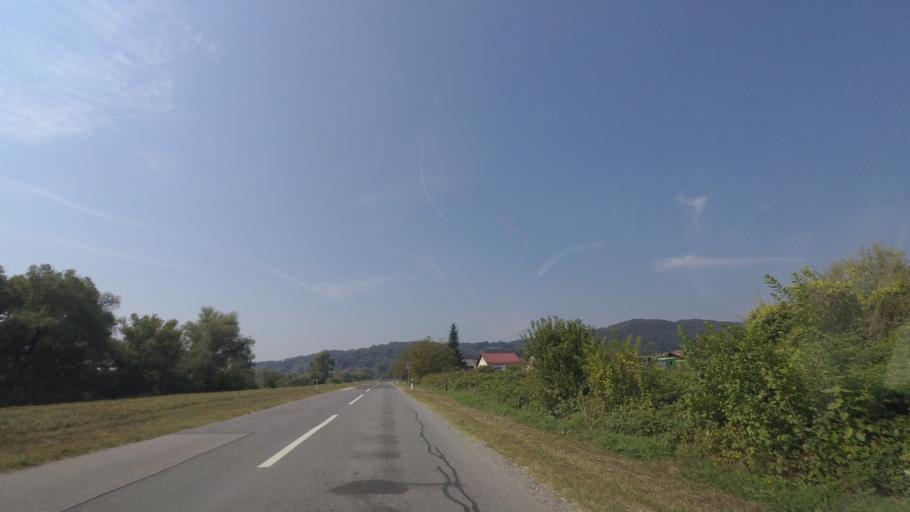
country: HR
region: Sisacko-Moslavacka
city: Dvor
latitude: 45.0684
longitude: 16.3818
